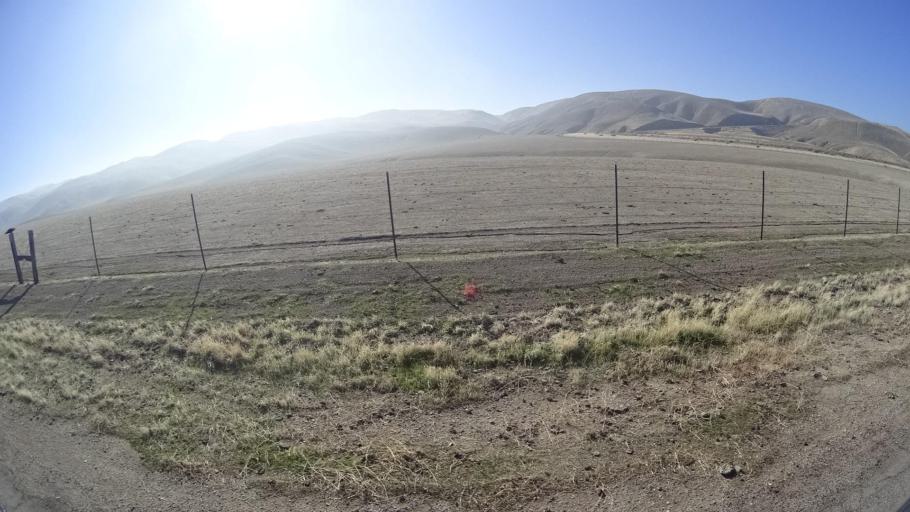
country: US
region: California
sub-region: Kern County
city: Maricopa
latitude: 35.0025
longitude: -119.4052
